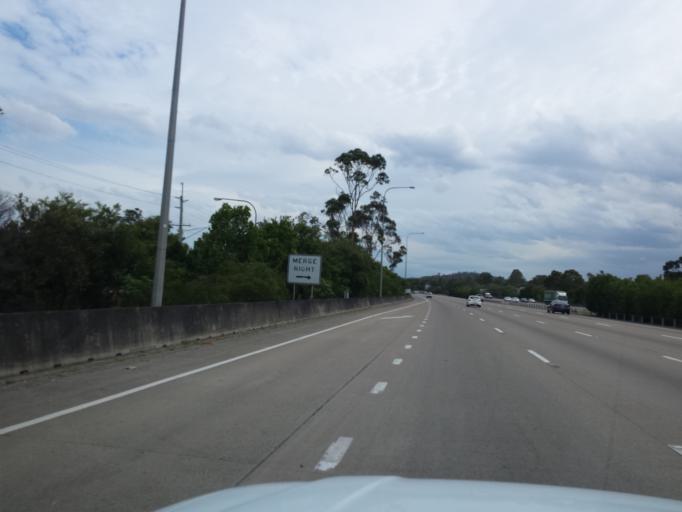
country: AU
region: Queensland
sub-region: Gold Coast
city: Oxenford
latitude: -27.8911
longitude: 153.3149
